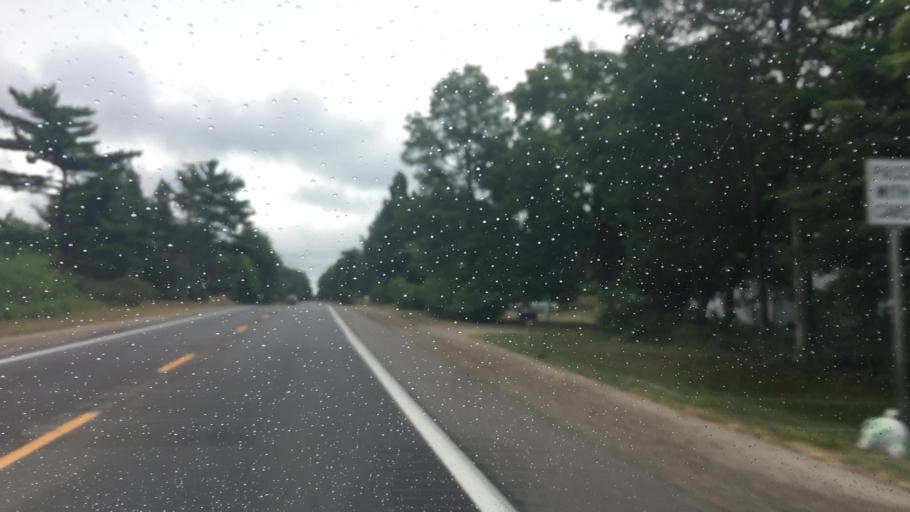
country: US
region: Michigan
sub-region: Ottawa County
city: Grand Haven
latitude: 42.9721
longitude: -86.1736
